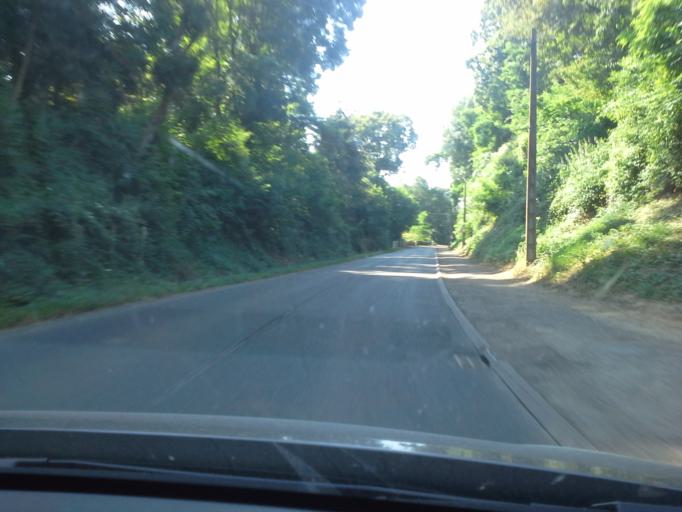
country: FR
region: Centre
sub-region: Departement du Loir-et-Cher
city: Chaumont-sur-Loire
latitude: 47.4780
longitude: 1.1899
